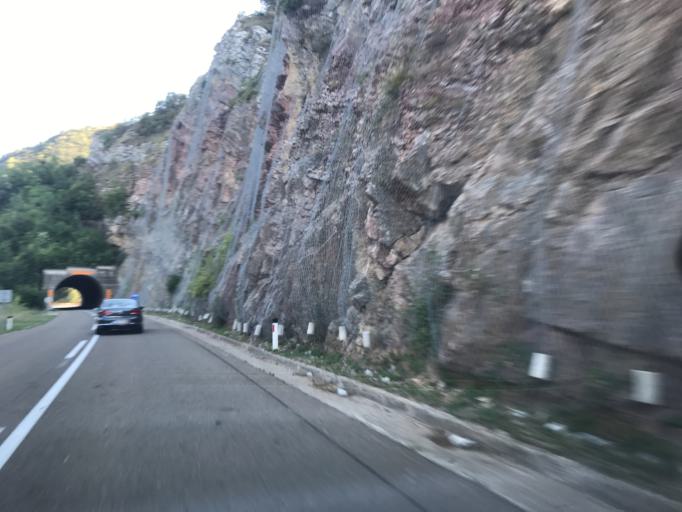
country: RO
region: Caras-Severin
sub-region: Comuna Berzasca
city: Berzasca
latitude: 44.5687
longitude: 22.0193
